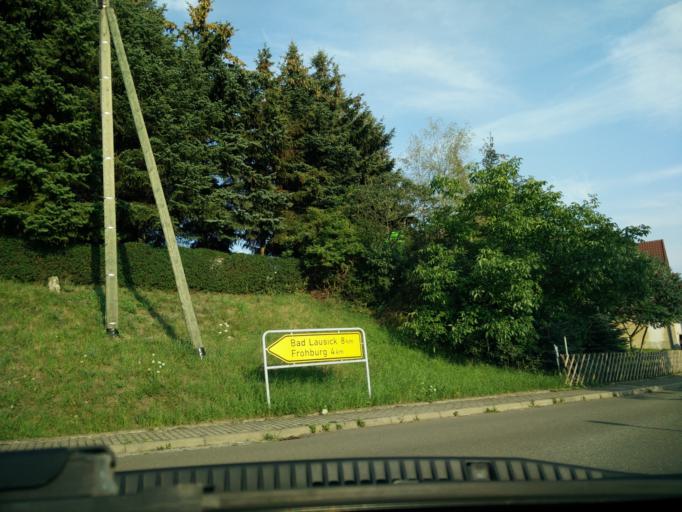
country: DE
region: Saxony
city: Frohburg
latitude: 51.0889
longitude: 12.5614
